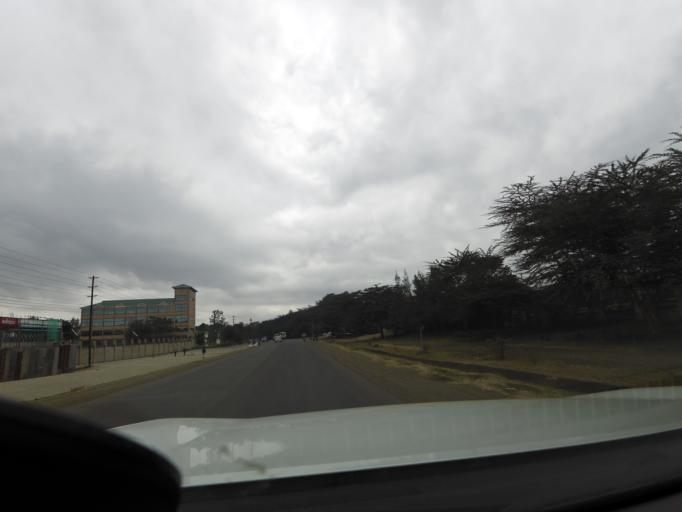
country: TZ
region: Arusha
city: Arusha
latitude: -3.3763
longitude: 36.6561
